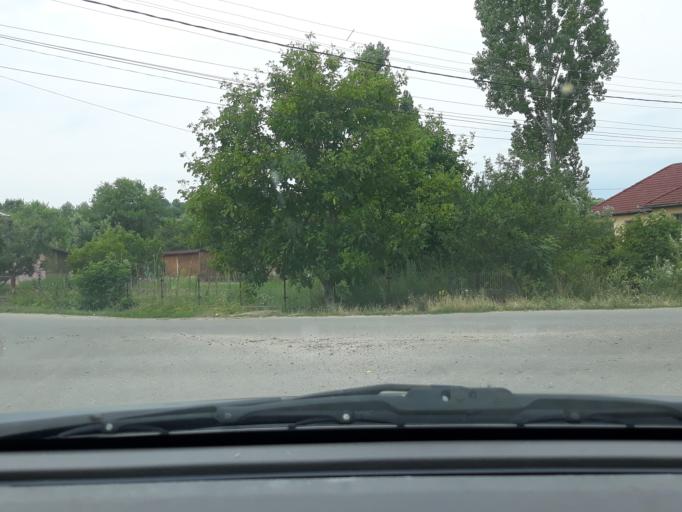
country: RO
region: Salaj
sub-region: Comuna Criseni
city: Criseni
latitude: 47.2570
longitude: 23.0625
